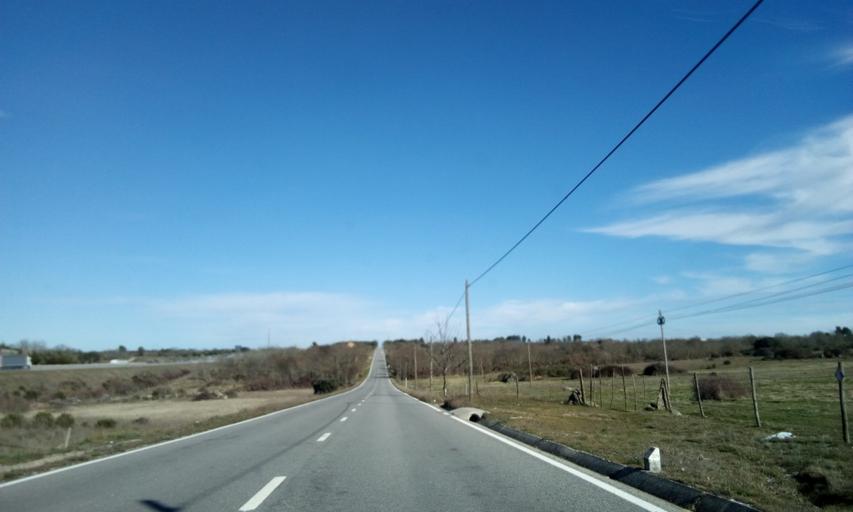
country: ES
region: Castille and Leon
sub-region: Provincia de Salamanca
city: Fuentes de Onoro
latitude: 40.6174
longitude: -6.8860
